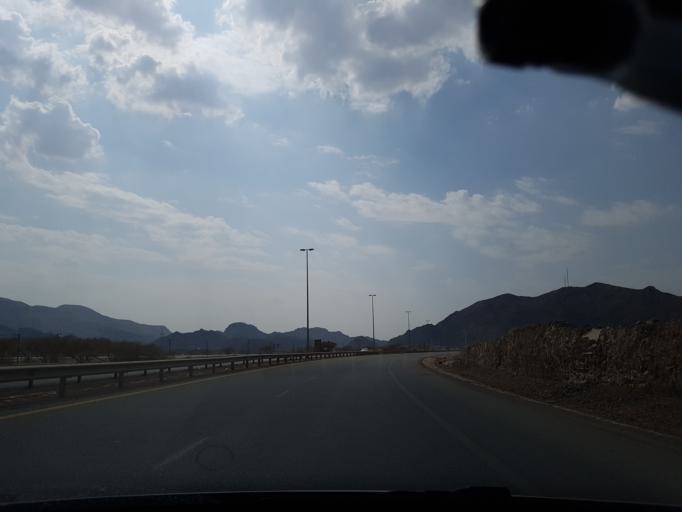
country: AE
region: Al Fujayrah
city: Dibba Al-Fujairah
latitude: 25.4995
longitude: 56.0703
